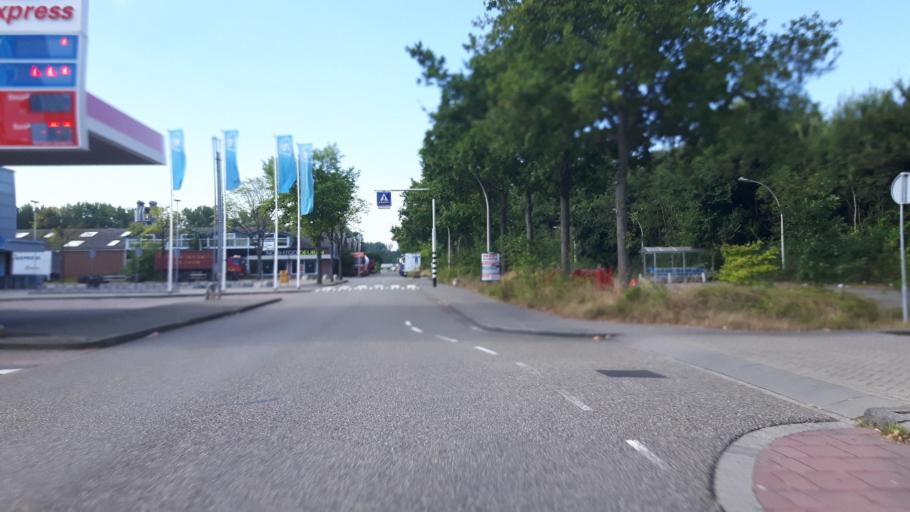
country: NL
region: South Holland
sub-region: Gemeente Katwijk
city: Katwijk aan den Rijn
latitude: 52.2027
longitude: 4.4274
